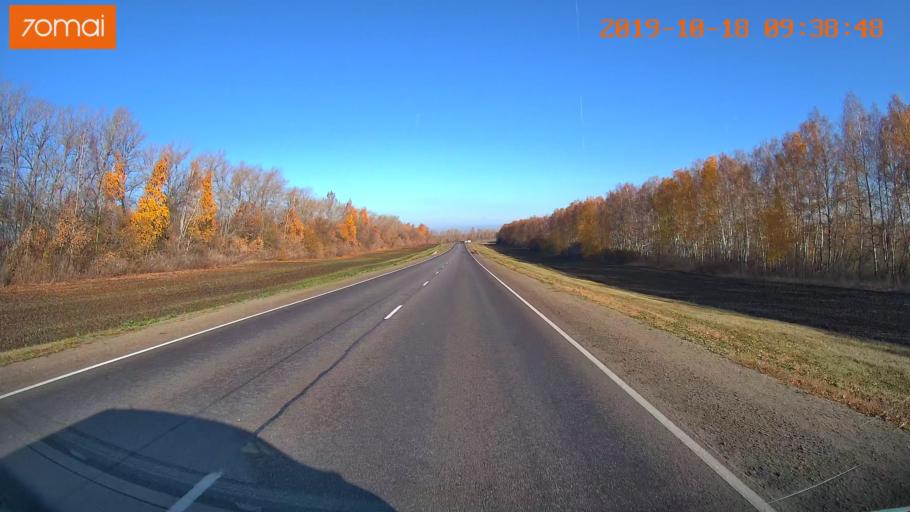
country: RU
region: Tula
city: Yefremov
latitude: 53.2435
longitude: 38.1356
